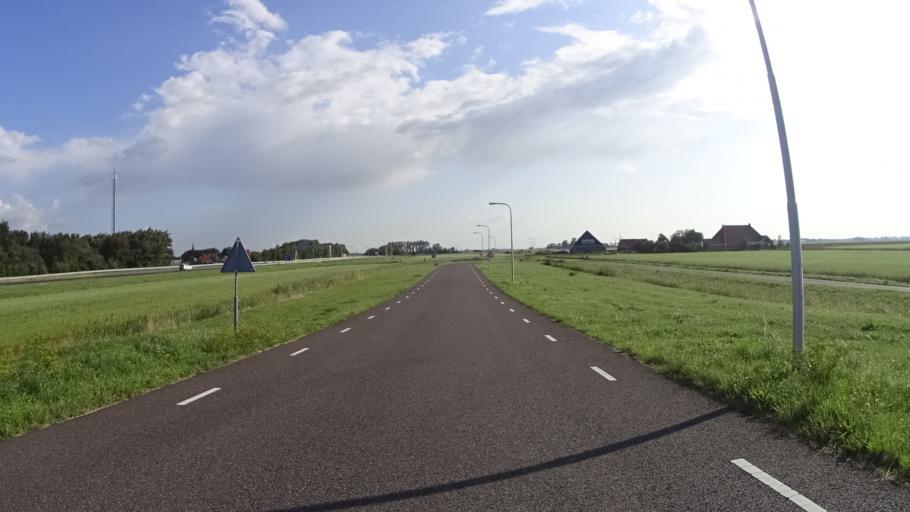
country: NL
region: Friesland
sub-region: Sudwest Fryslan
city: Makkum
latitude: 53.1064
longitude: 5.3915
